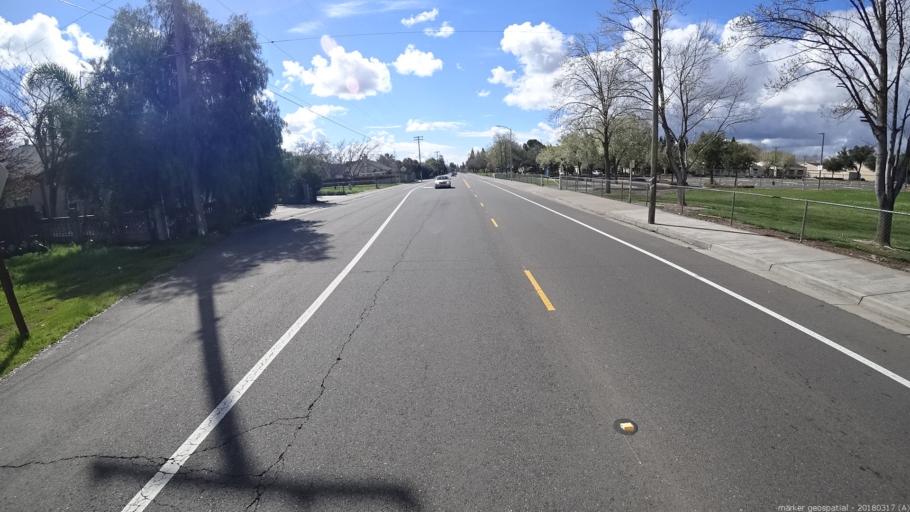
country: US
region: California
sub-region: Sacramento County
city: Florin
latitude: 38.4700
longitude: -121.3903
